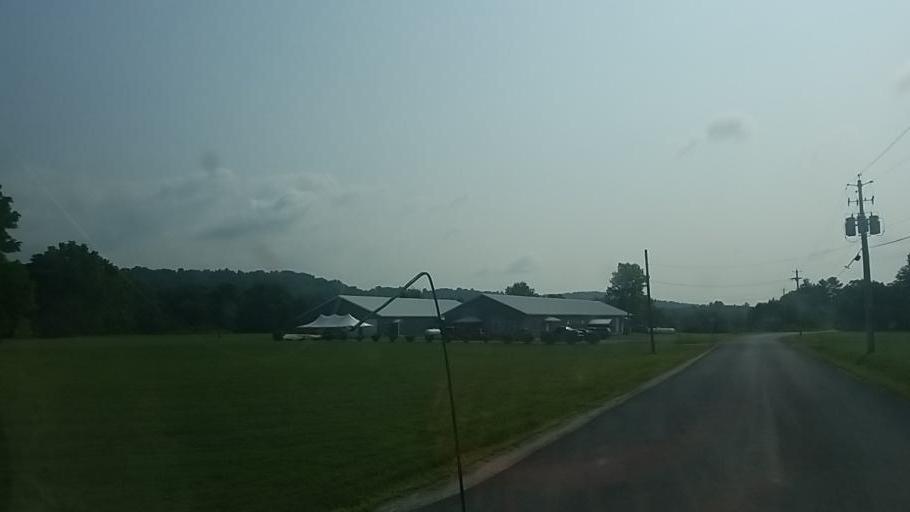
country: US
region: New York
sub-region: Montgomery County
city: Fonda
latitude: 42.9695
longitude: -74.4287
